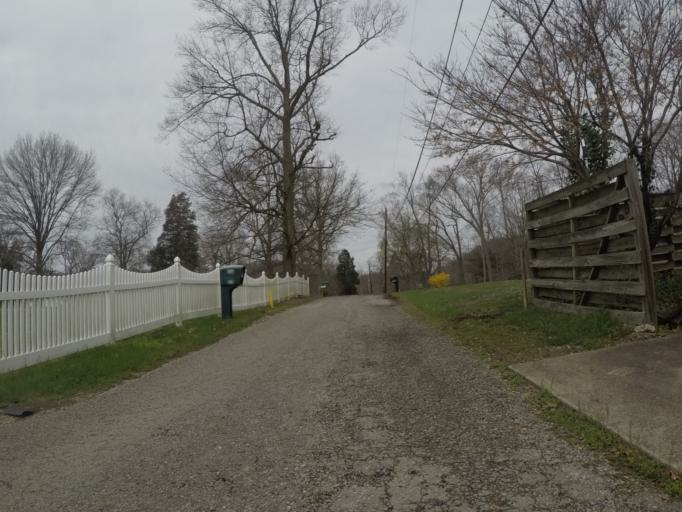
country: US
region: West Virginia
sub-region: Cabell County
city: Pea Ridge
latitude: 38.4242
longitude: -82.3176
